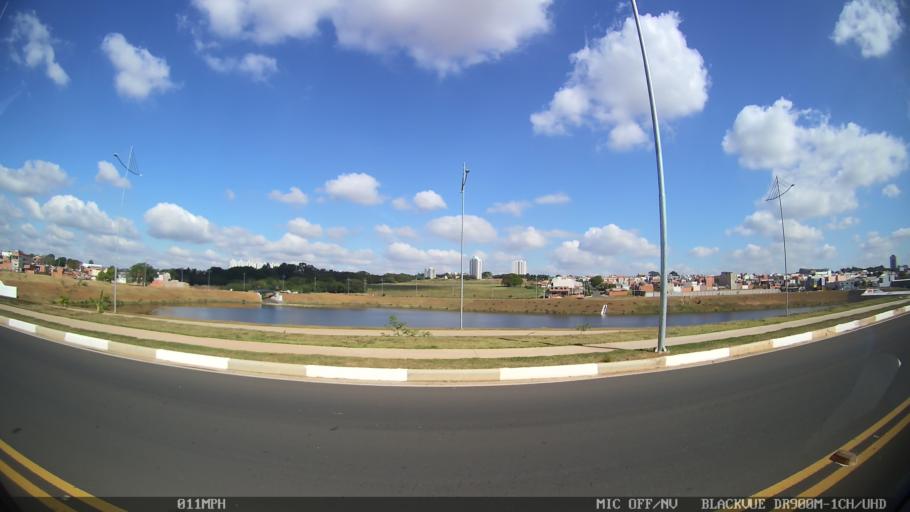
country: BR
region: Sao Paulo
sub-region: Hortolandia
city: Hortolandia
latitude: -22.8848
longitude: -47.2121
